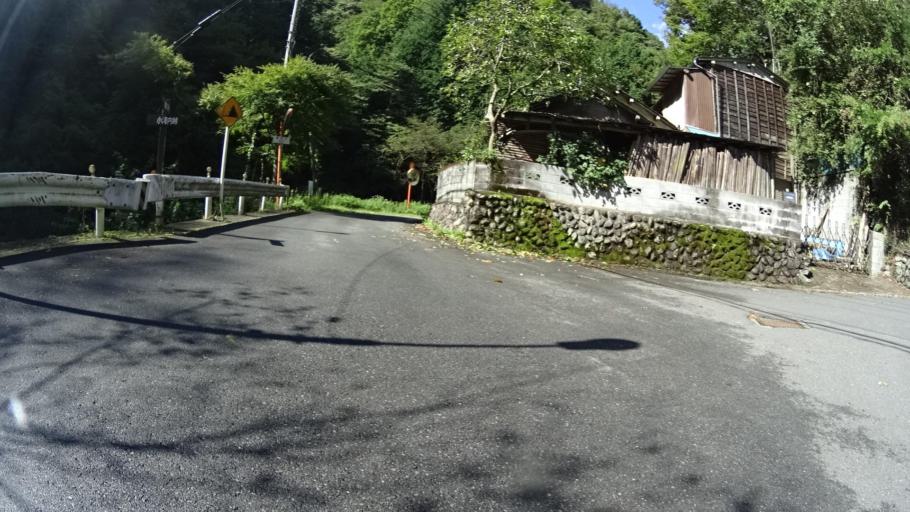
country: JP
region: Yamanashi
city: Uenohara
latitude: 35.7398
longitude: 139.0811
